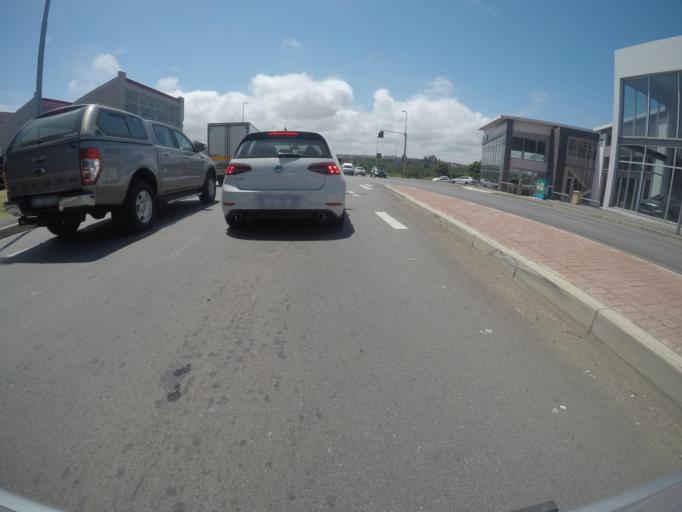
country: ZA
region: Eastern Cape
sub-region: Buffalo City Metropolitan Municipality
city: East London
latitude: -33.0079
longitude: 27.9138
